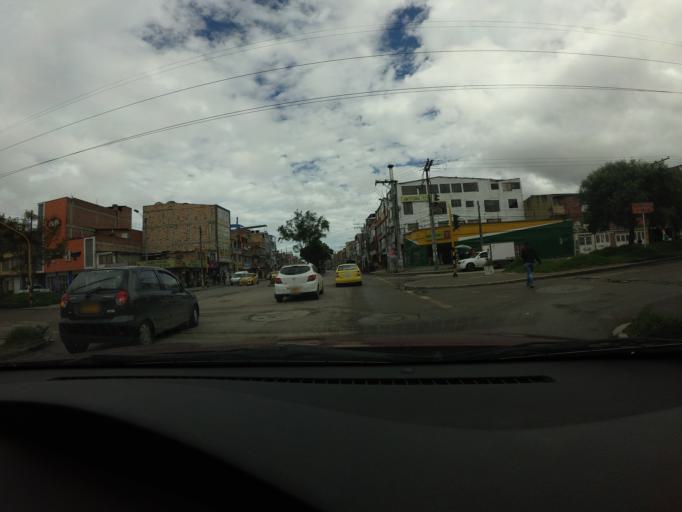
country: CO
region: Bogota D.C.
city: Bogota
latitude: 4.6034
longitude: -74.1507
